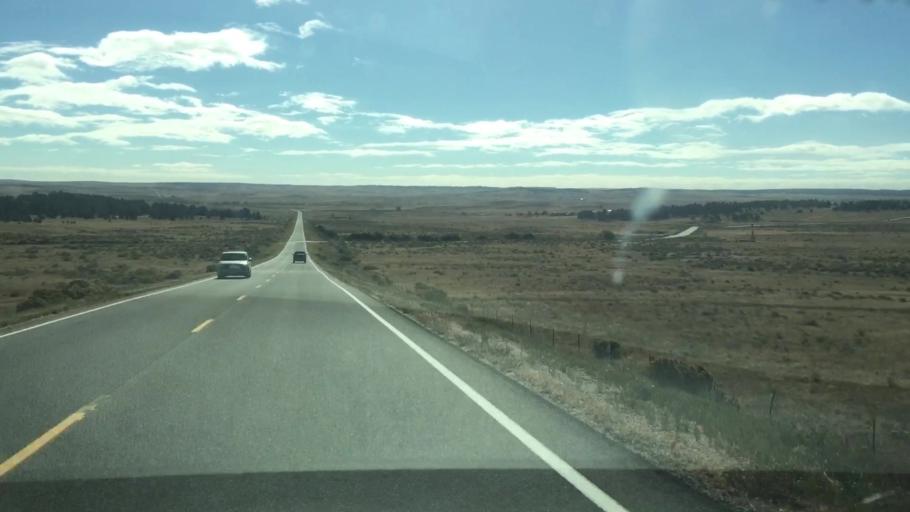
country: US
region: Colorado
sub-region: Elbert County
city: Kiowa
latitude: 39.3106
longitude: -104.3608
